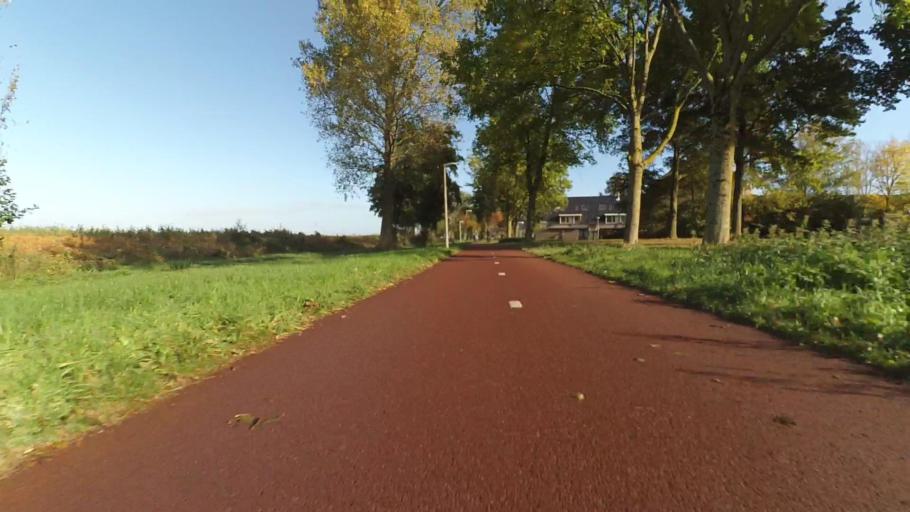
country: NL
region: Gelderland
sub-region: Gemeente Harderwijk
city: Harderwijk
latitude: 52.3432
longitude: 5.6086
